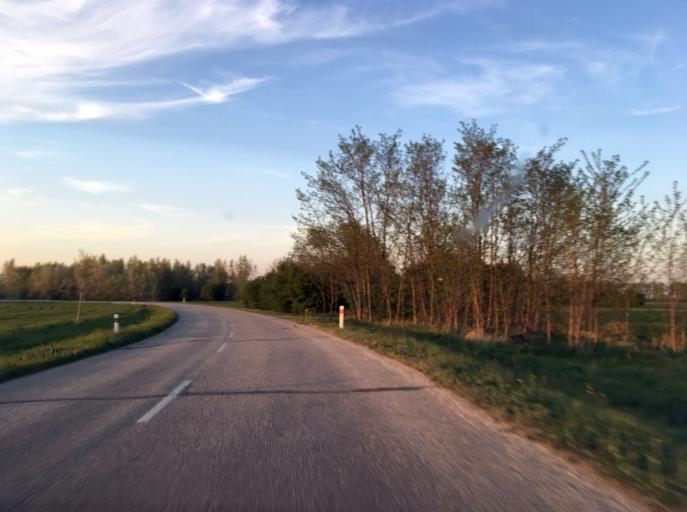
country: SK
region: Nitriansky
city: Kolarovo
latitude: 47.8848
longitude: 17.9241
